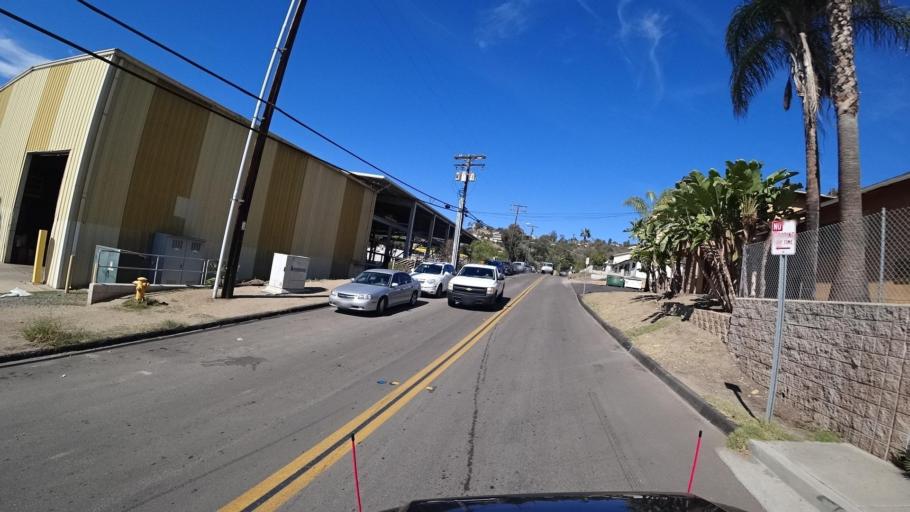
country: US
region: California
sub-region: San Diego County
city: La Presa
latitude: 32.7186
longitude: -117.0015
